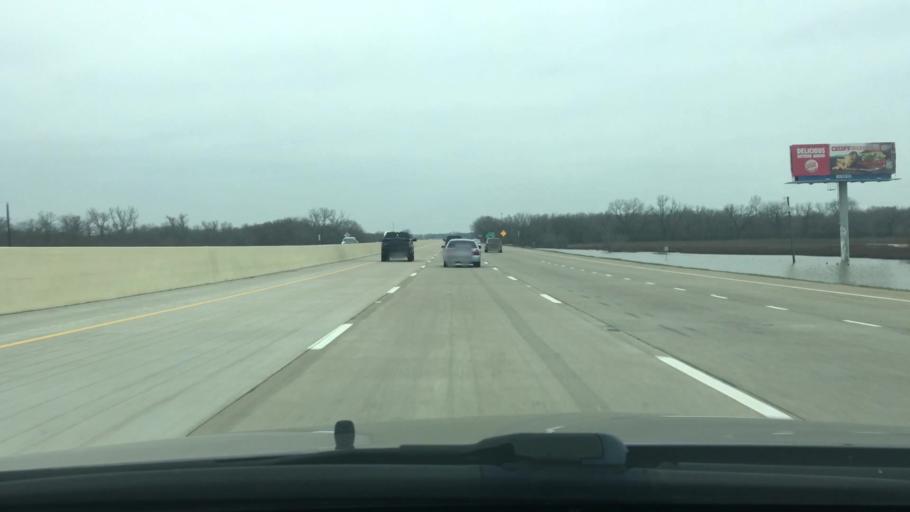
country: US
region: Texas
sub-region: Navarro County
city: Corsicana
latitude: 31.9541
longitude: -96.4211
